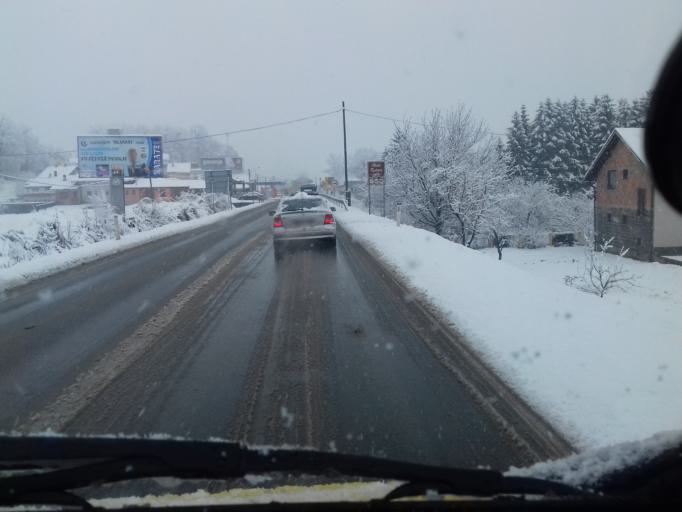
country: BA
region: Federation of Bosnia and Herzegovina
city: Vitez
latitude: 44.1522
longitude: 17.8027
